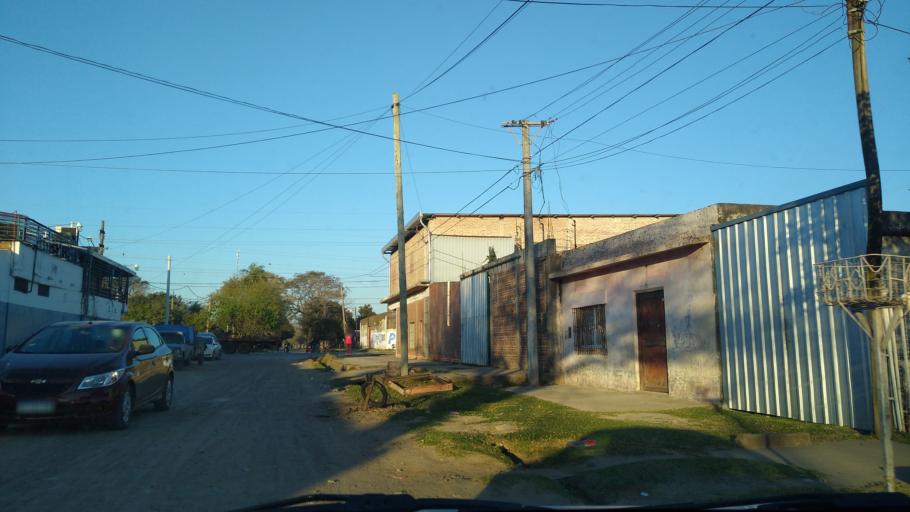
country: AR
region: Chaco
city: Resistencia
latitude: -27.4810
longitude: -58.9662
